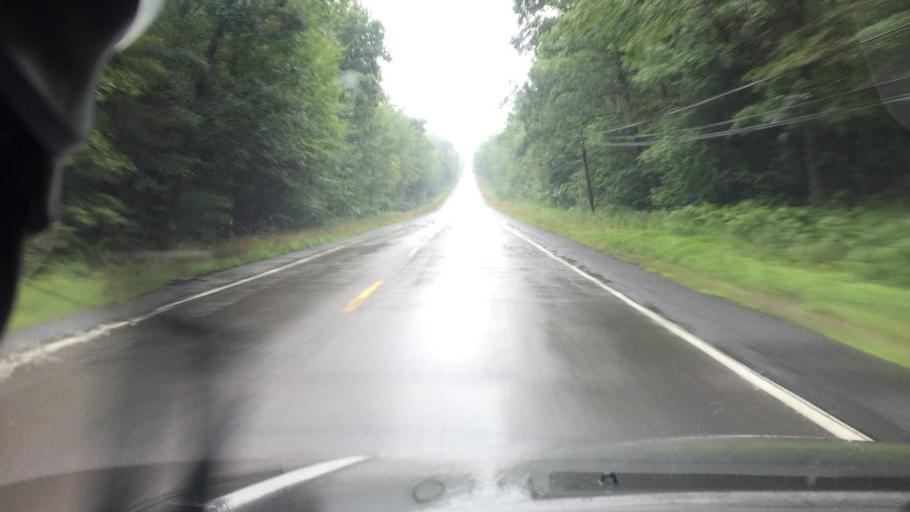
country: US
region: Pennsylvania
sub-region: Luzerne County
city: Freeland
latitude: 41.0296
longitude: -75.8561
